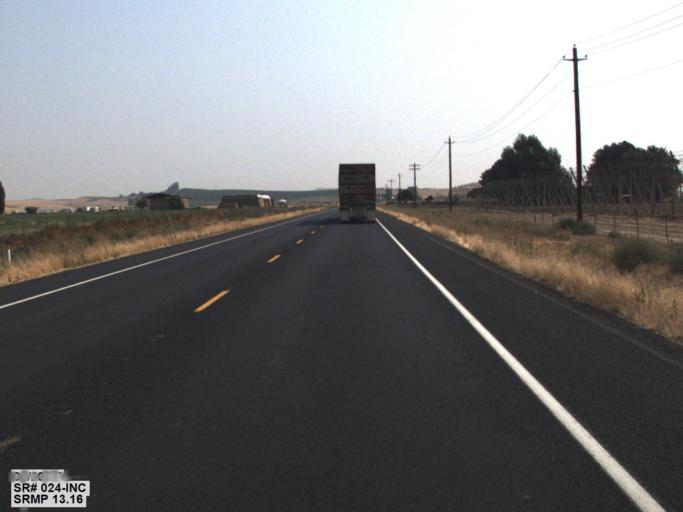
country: US
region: Washington
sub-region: Yakima County
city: Zillah
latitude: 46.5202
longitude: -120.2250
